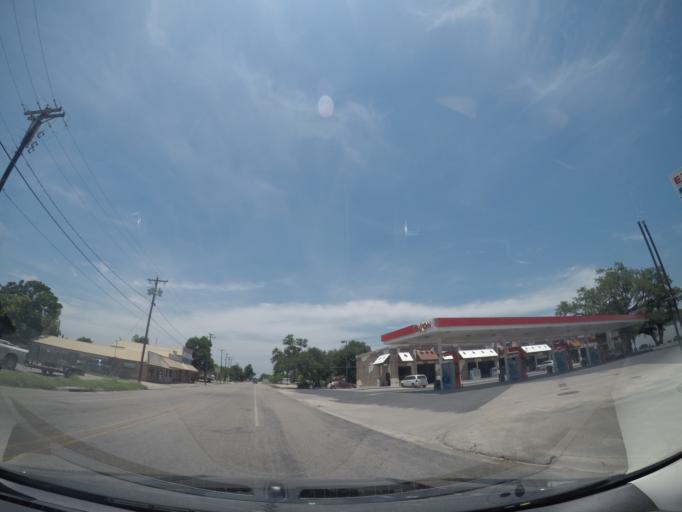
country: US
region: Texas
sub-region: Uvalde County
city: Uvalde
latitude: 29.2070
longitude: -99.7937
